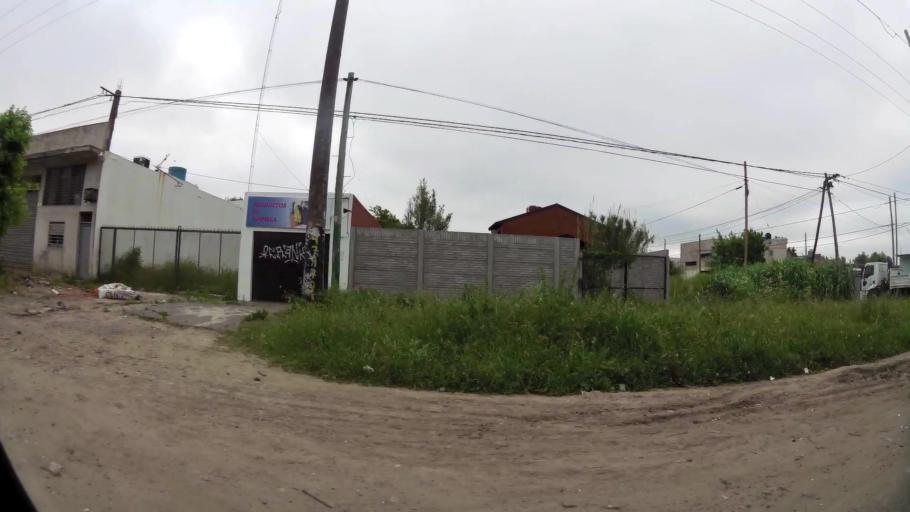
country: AR
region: Buenos Aires
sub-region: Partido de La Plata
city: La Plata
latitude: -34.9306
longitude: -57.9894
